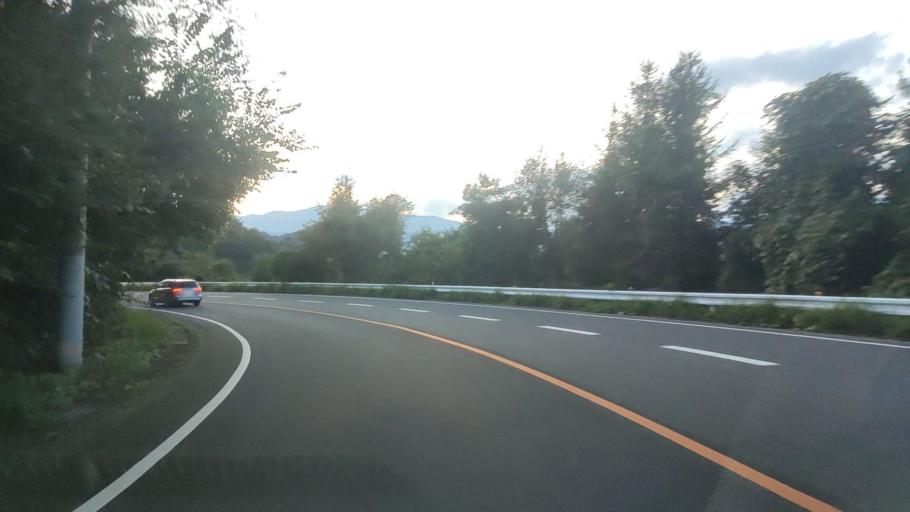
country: JP
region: Gunma
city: Nakanojomachi
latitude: 36.5413
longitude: 138.6128
